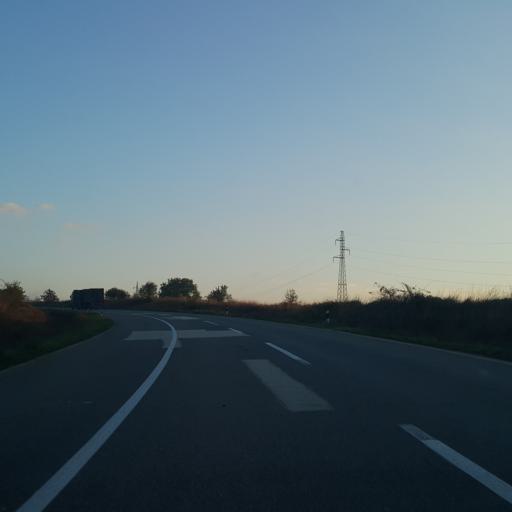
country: RS
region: Central Serbia
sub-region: Zajecarski Okrug
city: Zajecar
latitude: 44.0317
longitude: 22.3413
